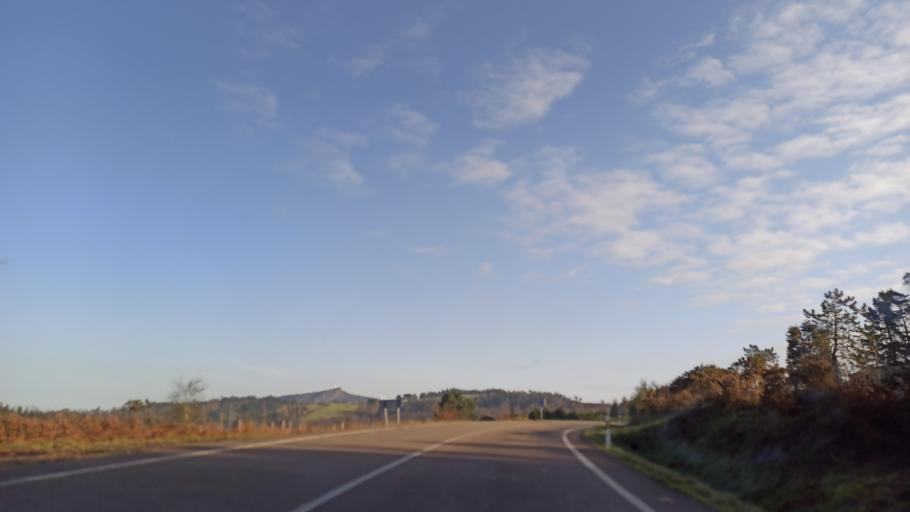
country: ES
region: Galicia
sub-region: Provincia da Coruna
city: As Pontes de Garcia Rodriguez
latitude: 43.4833
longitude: -7.8477
